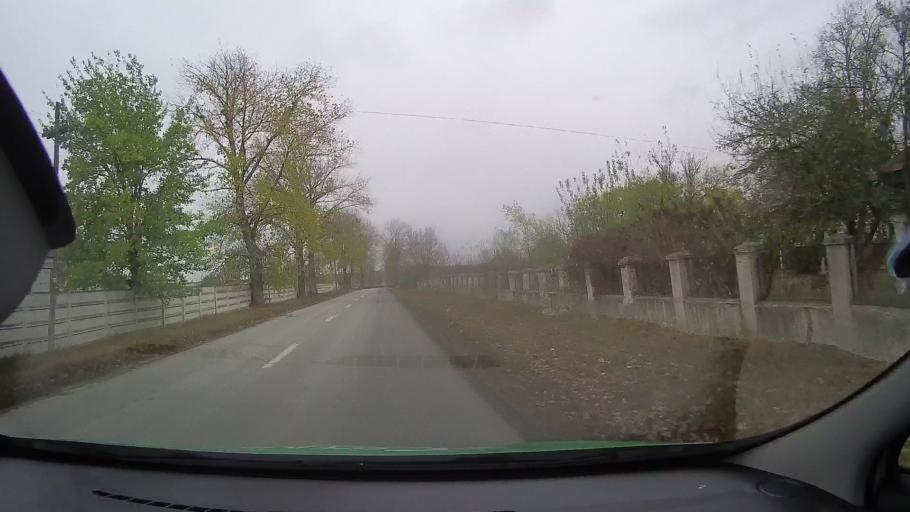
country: RO
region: Constanta
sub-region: Comuna Pantelimon
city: Pantelimon
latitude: 44.5500
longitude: 28.3290
